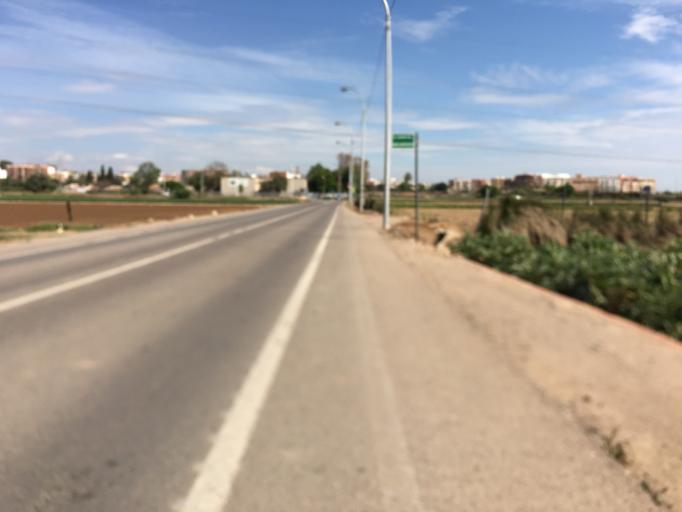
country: ES
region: Valencia
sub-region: Provincia de Valencia
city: Mislata
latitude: 39.4921
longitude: -0.4181
